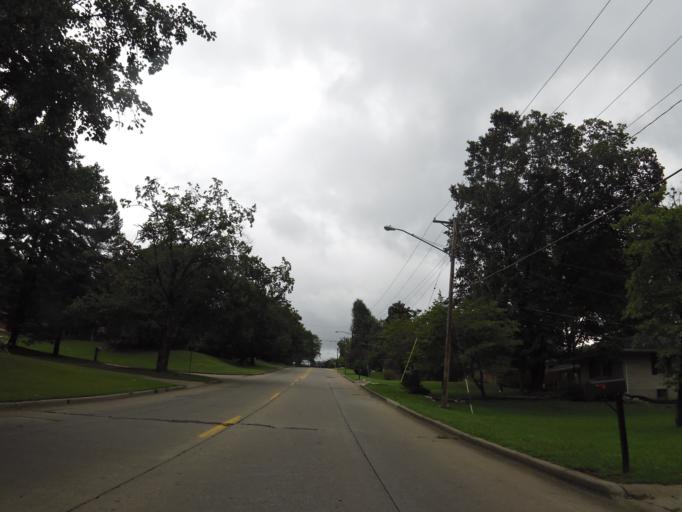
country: US
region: Missouri
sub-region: Cape Girardeau County
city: Cape Girardeau
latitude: 37.3275
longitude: -89.5489
